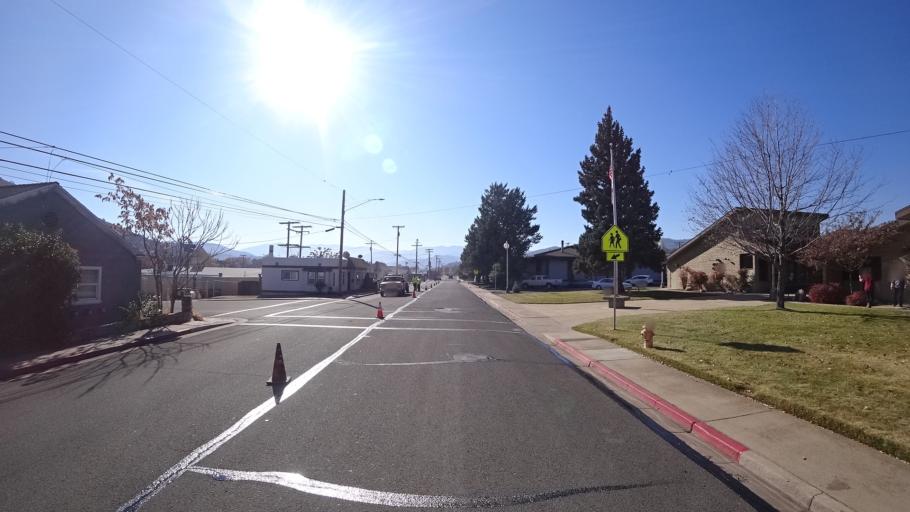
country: US
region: California
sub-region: Siskiyou County
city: Yreka
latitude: 41.7273
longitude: -122.6391
